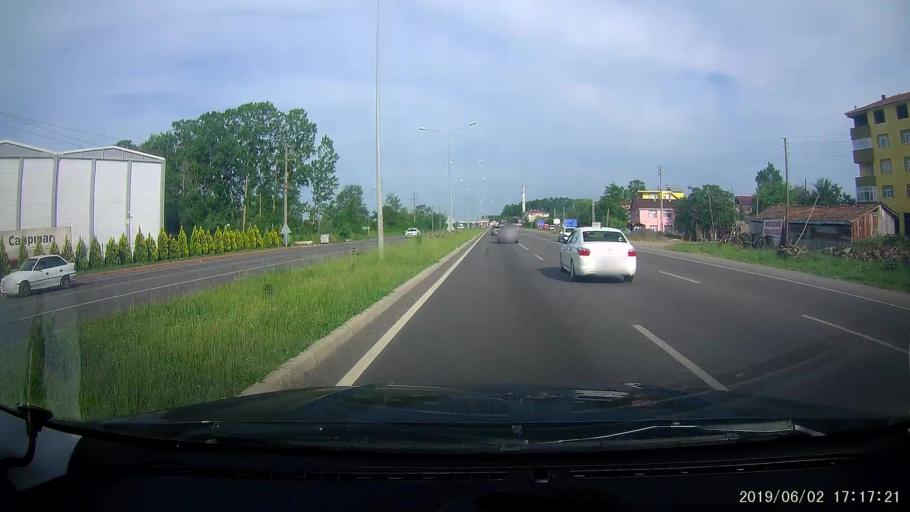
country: TR
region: Samsun
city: Dikbiyik
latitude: 41.2296
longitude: 36.5799
